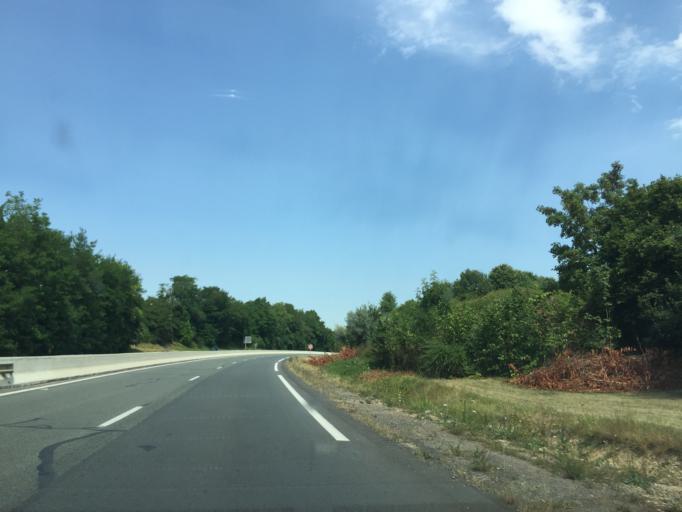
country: FR
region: Poitou-Charentes
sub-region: Departement de la Vienne
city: Biard
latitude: 46.5629
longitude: 0.3028
